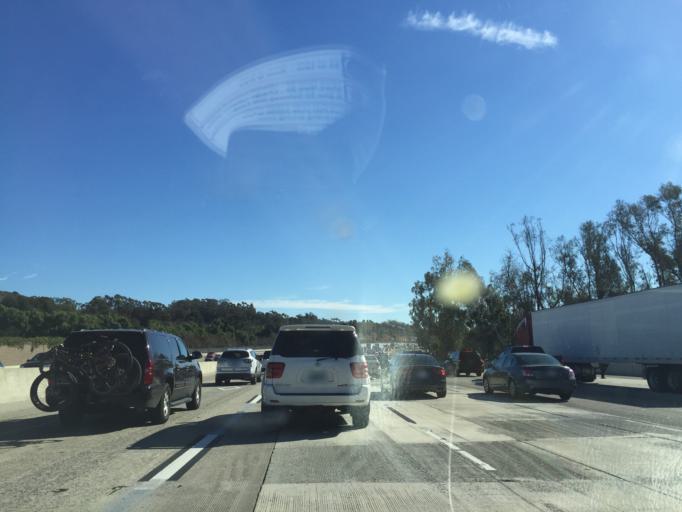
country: US
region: California
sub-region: Orange County
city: San Juan Capistrano
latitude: 33.5286
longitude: -117.6715
